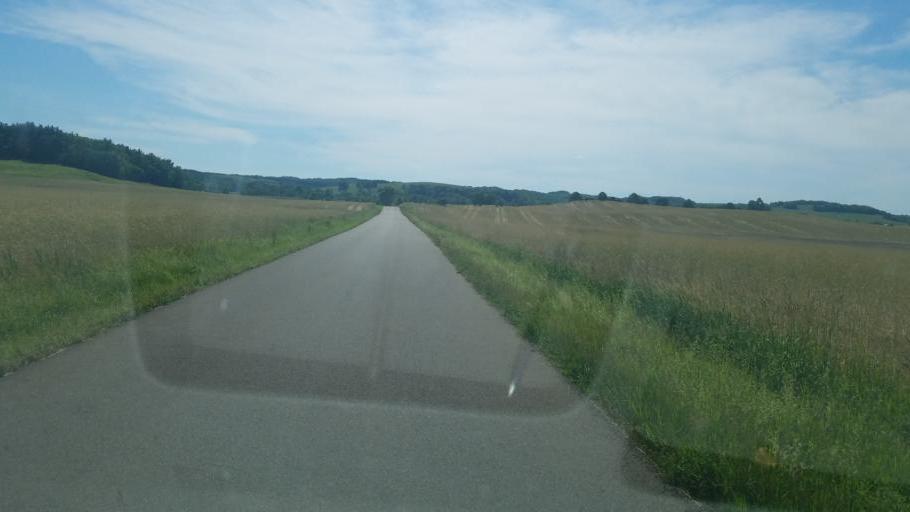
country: US
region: Ohio
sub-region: Coshocton County
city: West Lafayette
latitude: 40.2359
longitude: -81.7191
